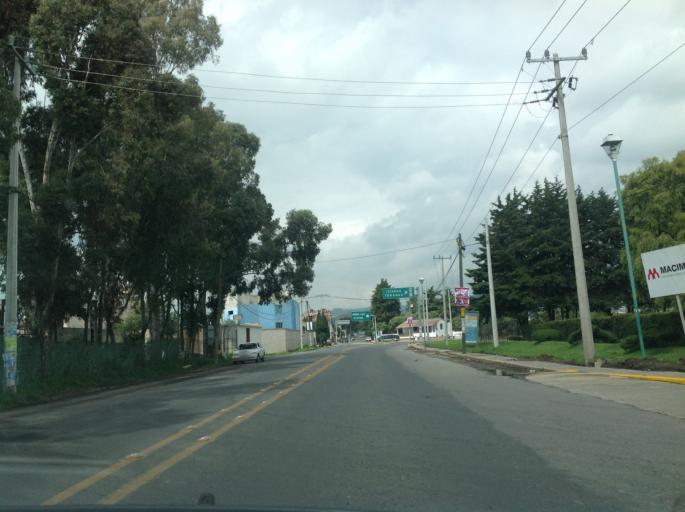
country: MX
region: Morelos
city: Tenango de Arista
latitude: 19.1058
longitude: -99.5788
